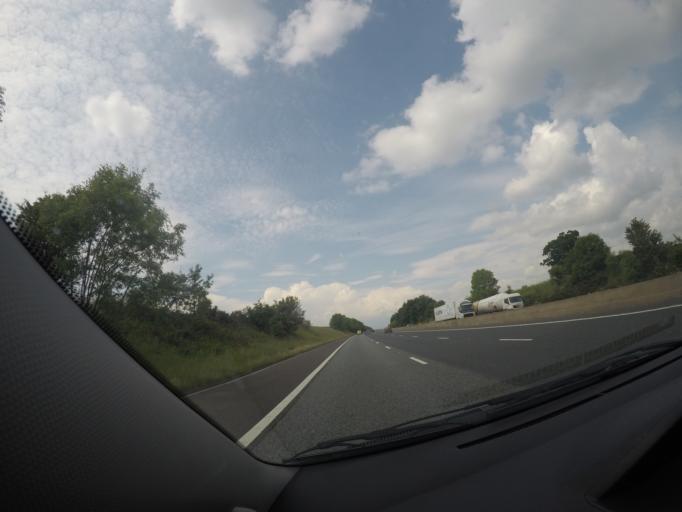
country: GB
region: England
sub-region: Cumbria
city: Scotby
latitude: 54.8270
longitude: -2.8894
